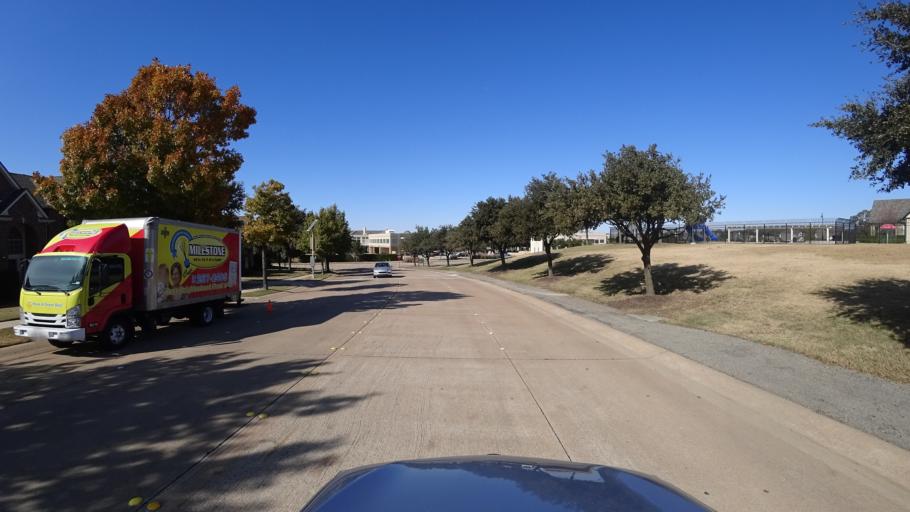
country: US
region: Texas
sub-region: Denton County
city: The Colony
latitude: 33.0327
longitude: -96.8975
